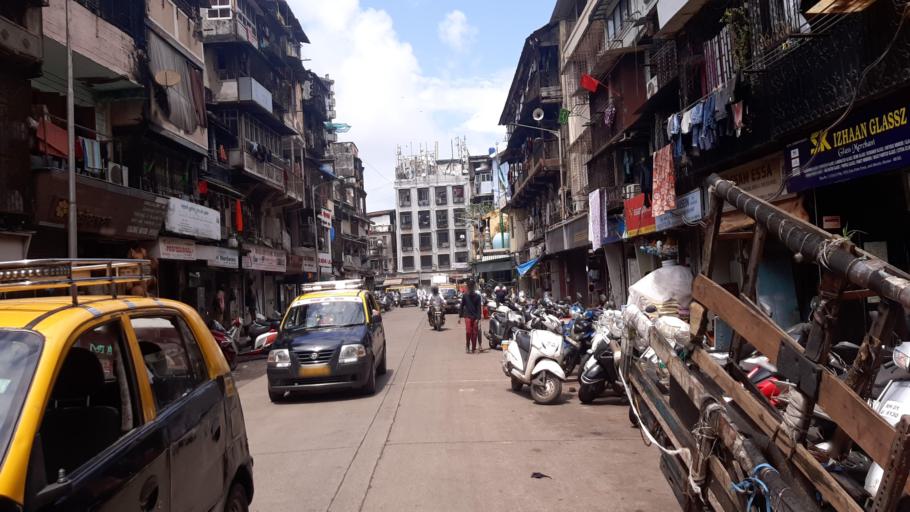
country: IN
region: Maharashtra
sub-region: Mumbai Suburban
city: Mumbai
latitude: 18.9562
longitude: 72.8294
